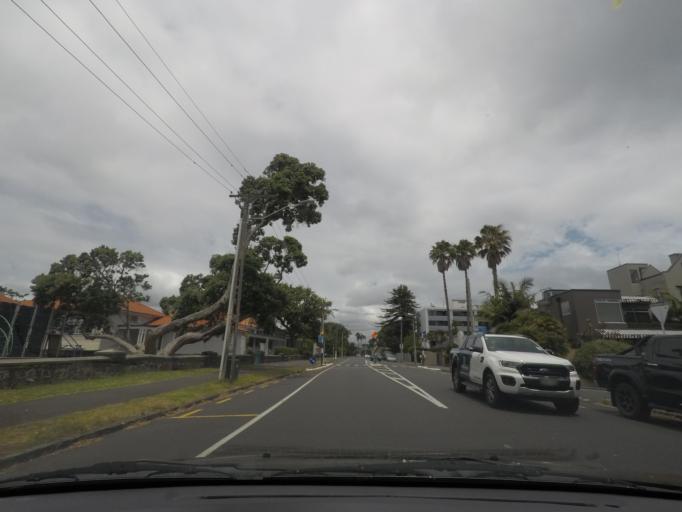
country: NZ
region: Auckland
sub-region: Auckland
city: Auckland
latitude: -36.8547
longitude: 174.7869
